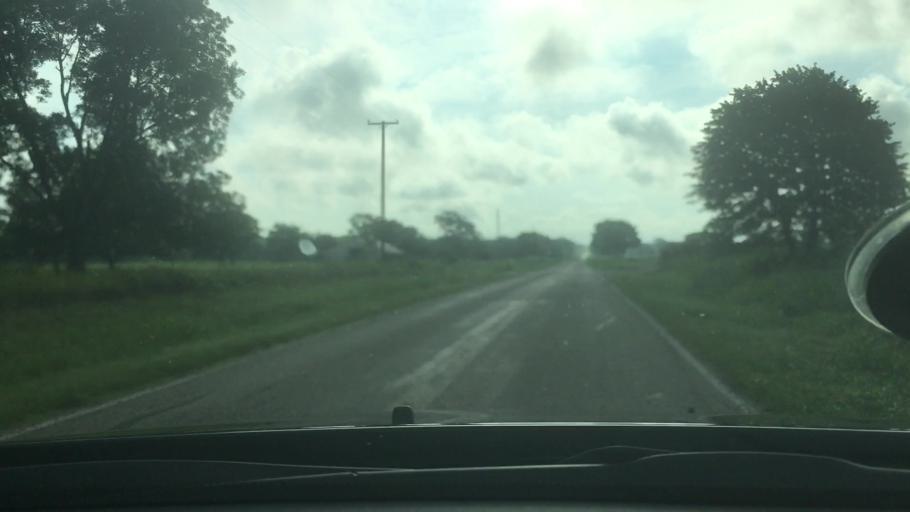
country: US
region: Oklahoma
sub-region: Pontotoc County
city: Ada
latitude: 34.6945
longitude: -96.5526
